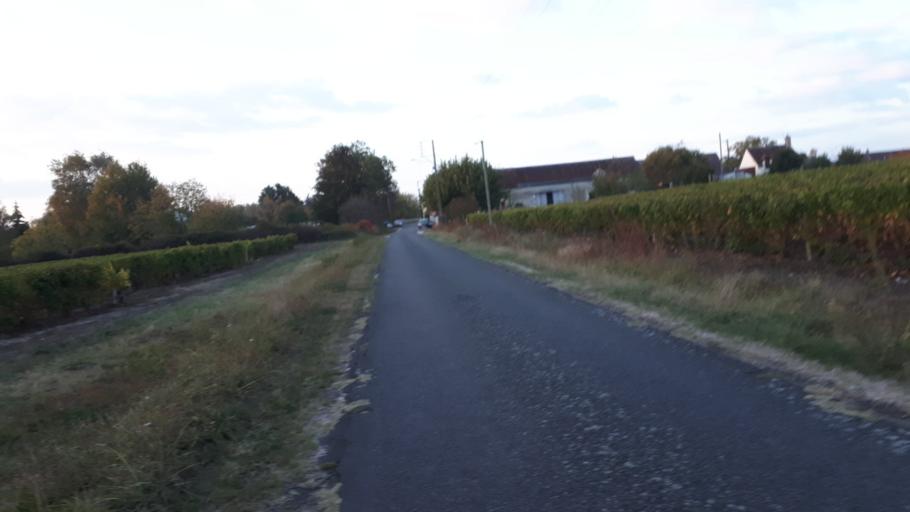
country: FR
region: Centre
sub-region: Departement du Loir-et-Cher
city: Saint-Romain-sur-Cher
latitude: 47.3626
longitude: 1.4071
